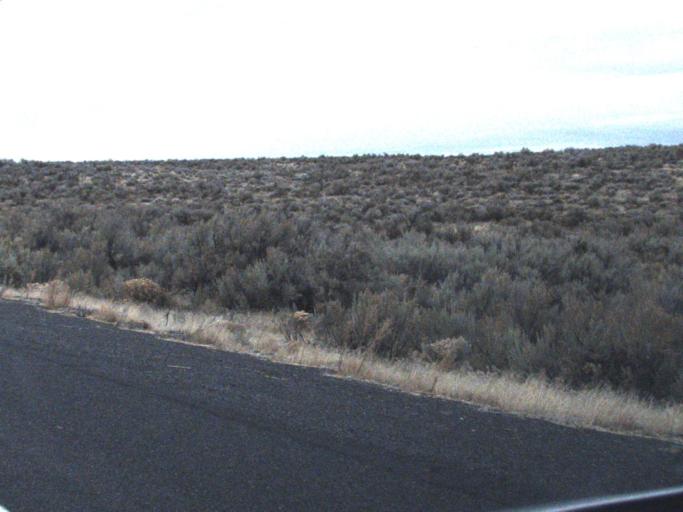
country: US
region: Washington
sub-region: Adams County
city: Ritzville
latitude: 46.7953
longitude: -118.5150
